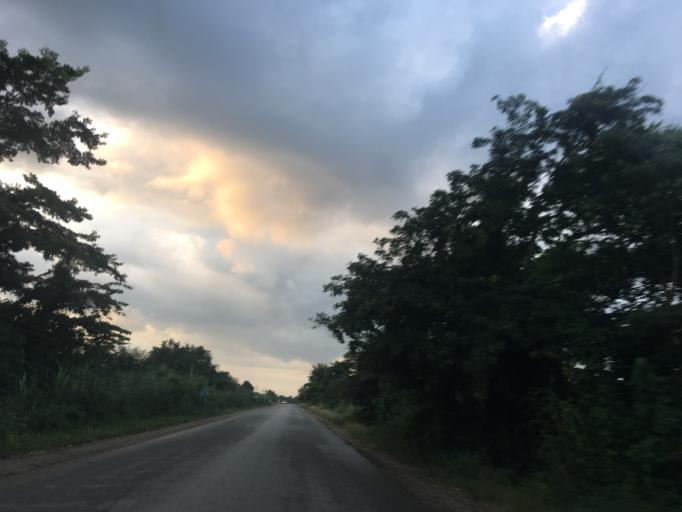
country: GH
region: Western
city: Bibiani
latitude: 6.7522
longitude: -2.5045
